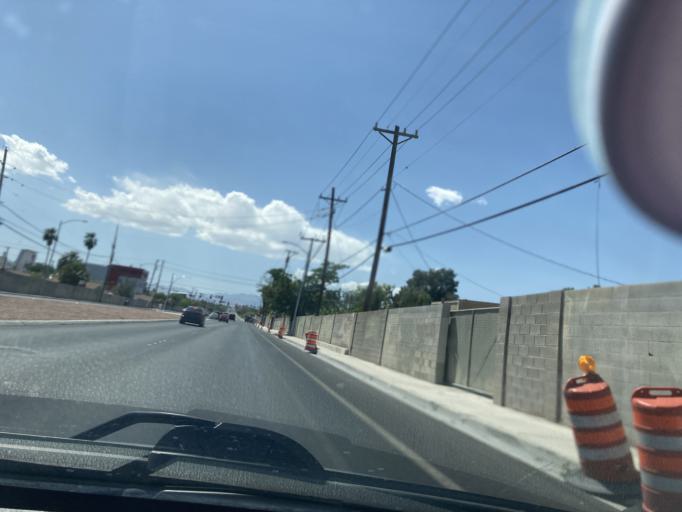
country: US
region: Nevada
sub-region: Clark County
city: North Las Vegas
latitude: 36.1812
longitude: -115.1137
